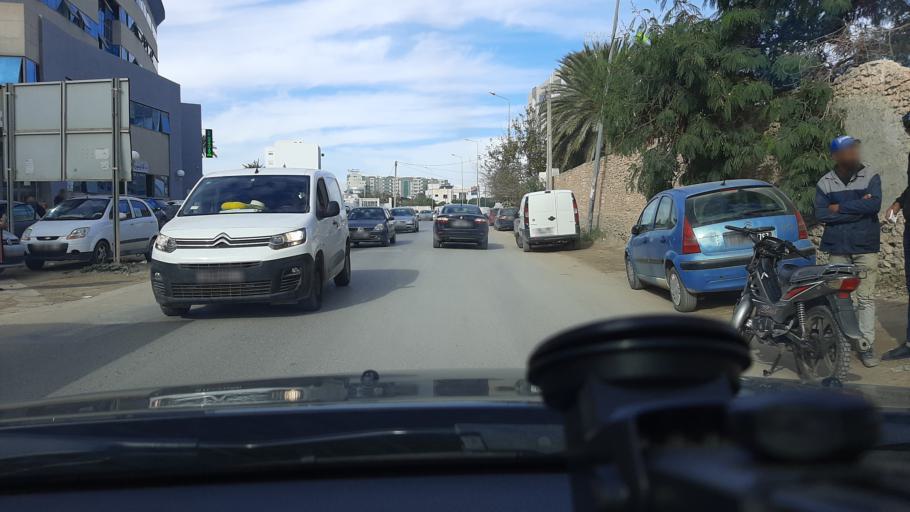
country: TN
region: Safaqis
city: Sfax
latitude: 34.7581
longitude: 10.7335
